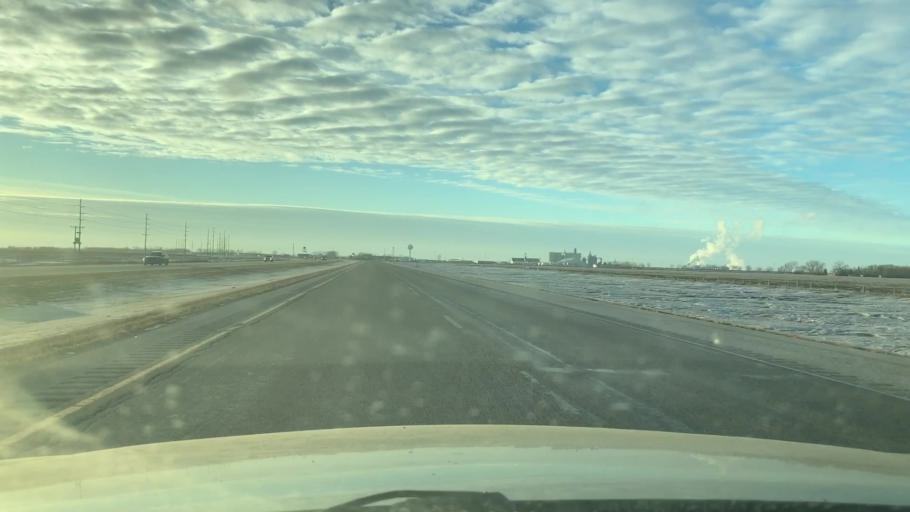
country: US
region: North Dakota
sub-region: Cass County
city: Casselton
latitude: 46.8768
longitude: -97.1849
